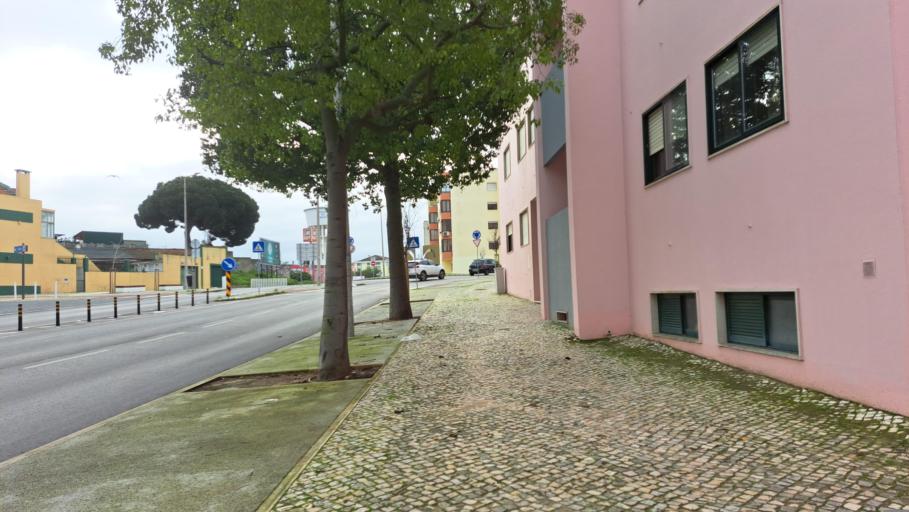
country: PT
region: Setubal
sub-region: Moita
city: Alhos Vedros
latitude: 38.6554
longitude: -9.0480
